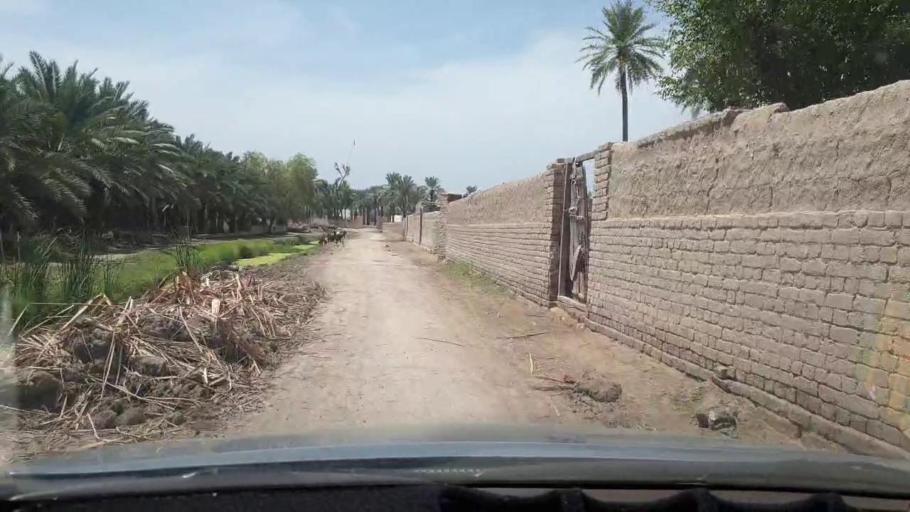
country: PK
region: Sindh
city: Khairpur
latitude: 27.4788
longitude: 68.7679
